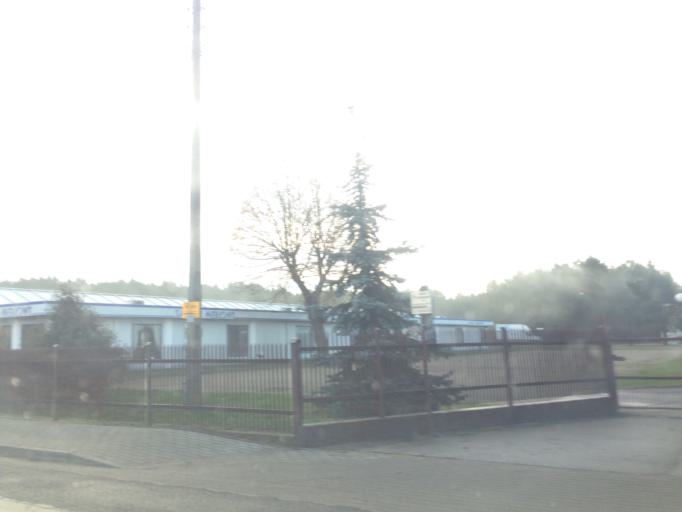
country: PL
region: Kujawsko-Pomorskie
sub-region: Powiat torunski
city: Wielka Nieszawka
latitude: 52.9927
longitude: 18.4598
